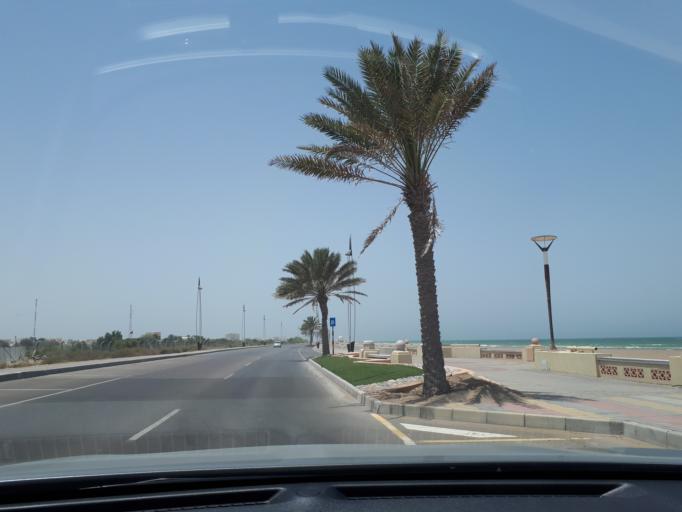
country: OM
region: Muhafazat Masqat
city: As Sib al Jadidah
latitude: 23.6474
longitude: 58.2367
